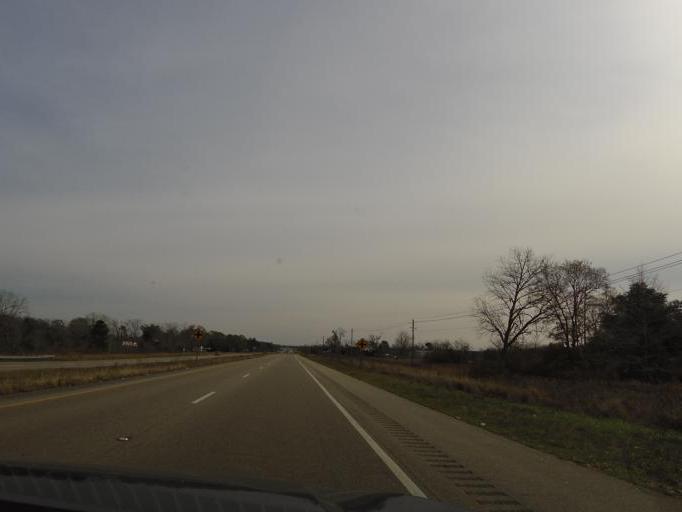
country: US
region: Alabama
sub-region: Houston County
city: Ashford
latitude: 31.1549
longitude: -85.1804
